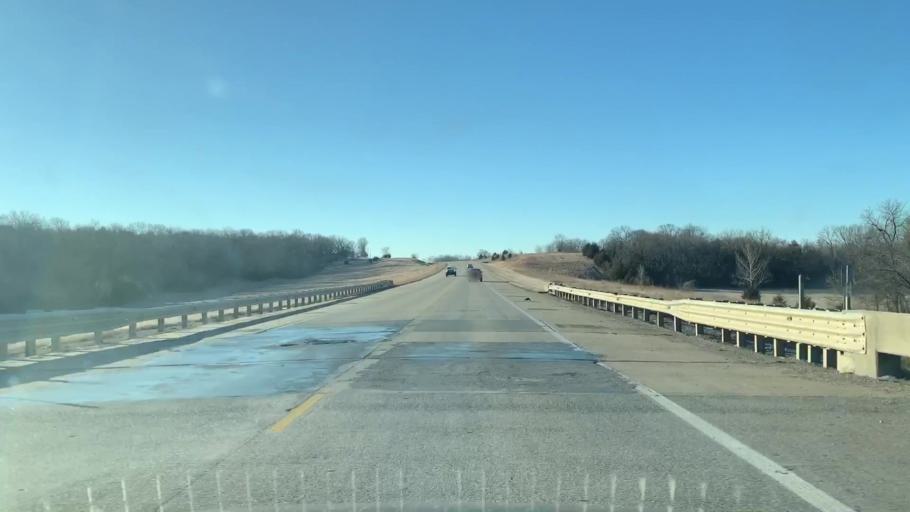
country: US
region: Kansas
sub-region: Crawford County
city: Arma
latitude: 37.5838
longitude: -94.7056
